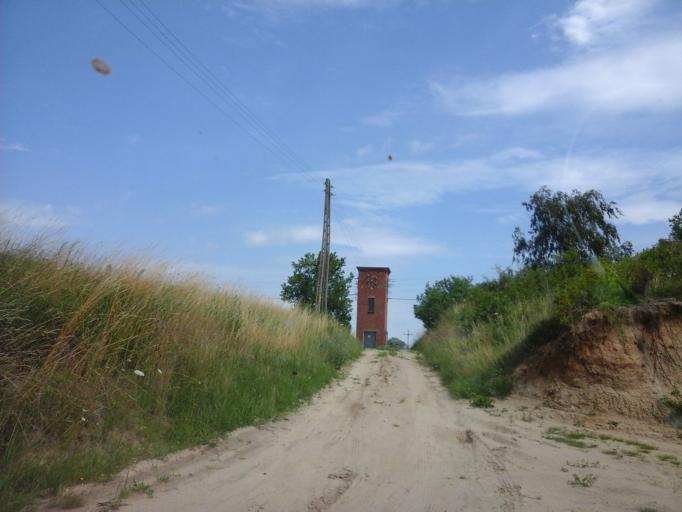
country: PL
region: West Pomeranian Voivodeship
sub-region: Powiat choszczenski
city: Bierzwnik
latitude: 53.0208
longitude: 15.6991
